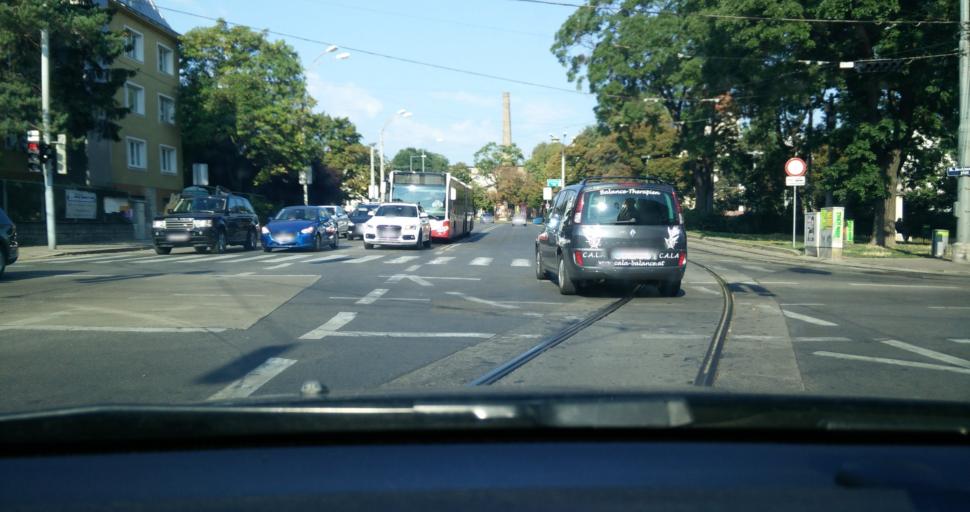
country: AT
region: Vienna
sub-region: Wien Stadt
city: Vienna
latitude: 48.2085
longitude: 16.3049
